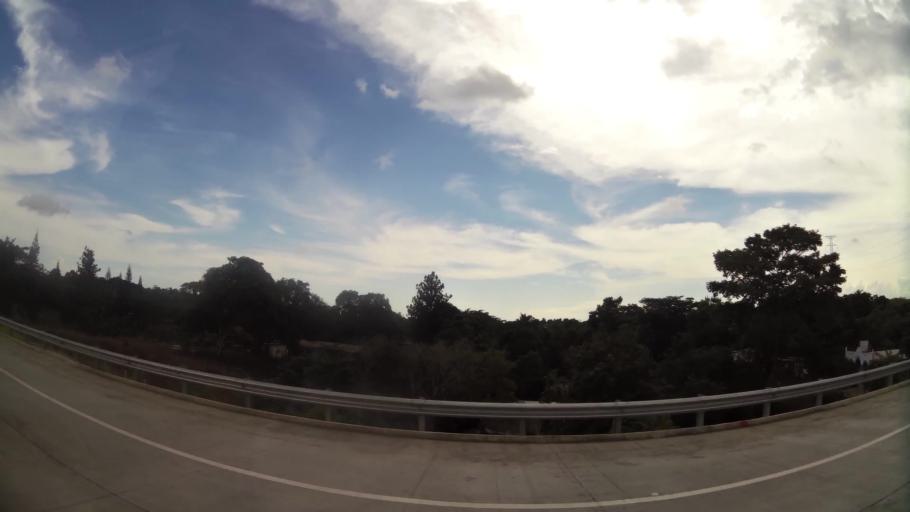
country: PA
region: Panama
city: Tocumen
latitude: 9.1097
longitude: -79.4041
